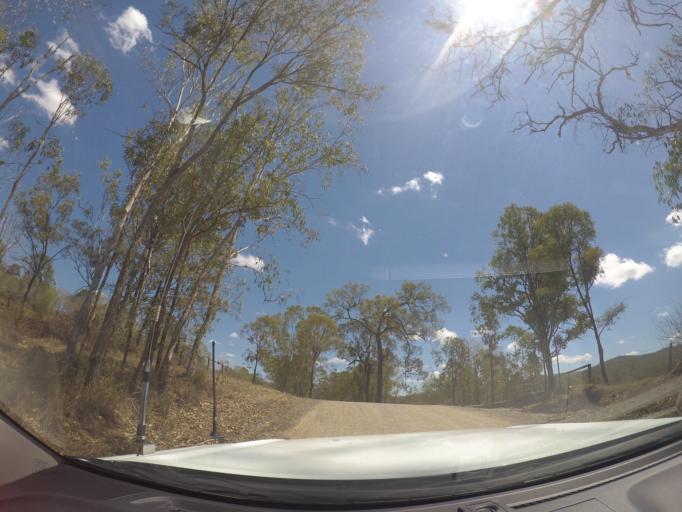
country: AU
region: Queensland
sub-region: Logan
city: North Maclean
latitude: -27.8351
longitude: 152.8697
